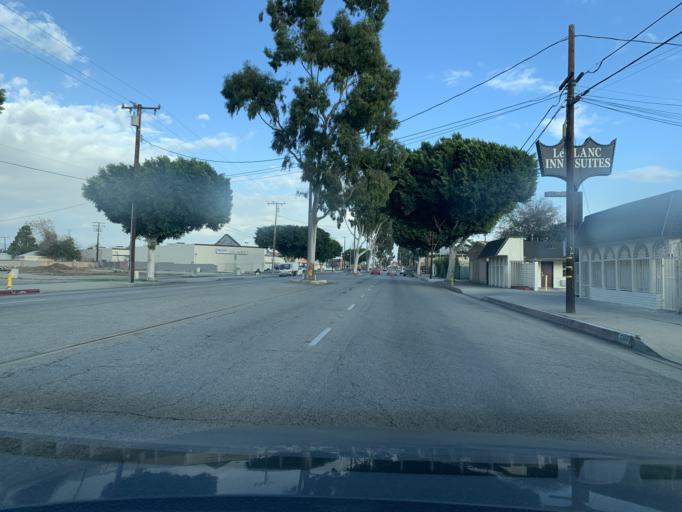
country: US
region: California
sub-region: Los Angeles County
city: El Monte
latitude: 34.0628
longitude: -118.0250
